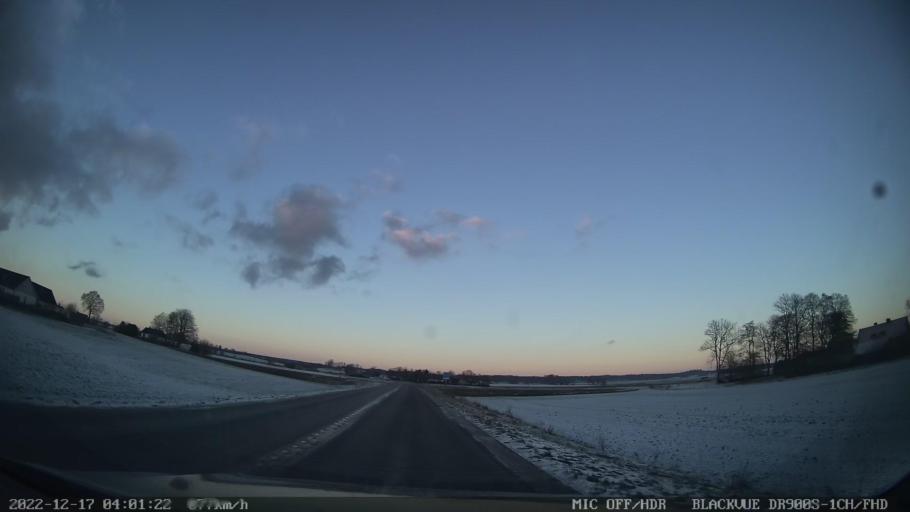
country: SE
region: Skane
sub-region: Simrishamns Kommun
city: Kivik
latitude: 55.5804
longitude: 14.1235
